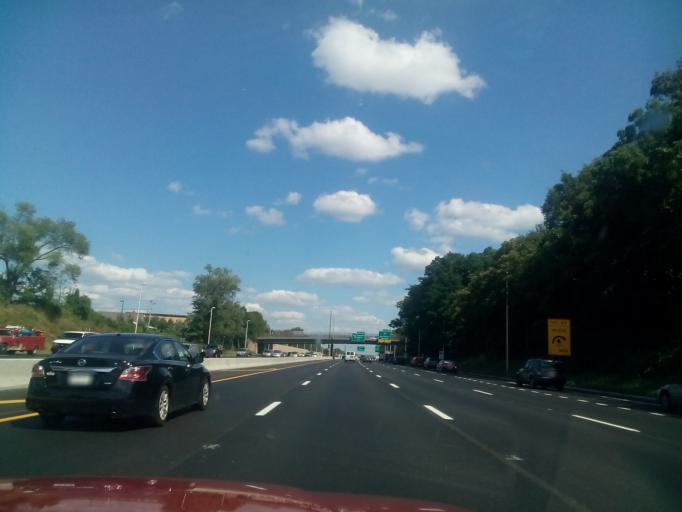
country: US
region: New Jersey
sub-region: Morris County
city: Parsippany
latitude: 40.8653
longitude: -74.4267
